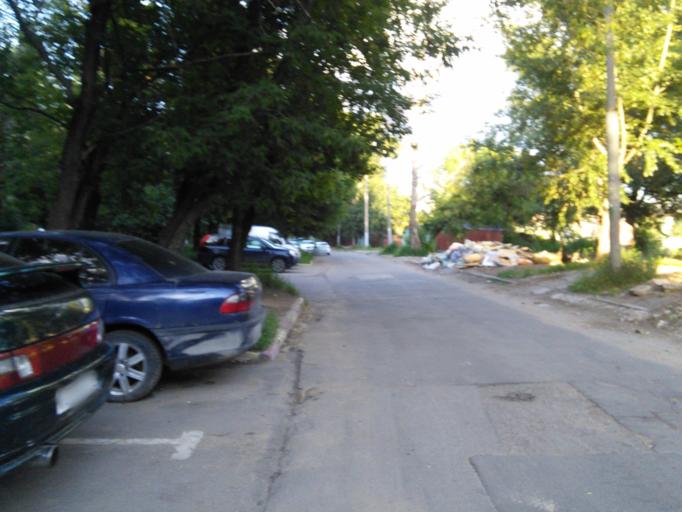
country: RU
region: Moscow
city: Novyye Cheremushki
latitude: 55.6900
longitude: 37.6076
